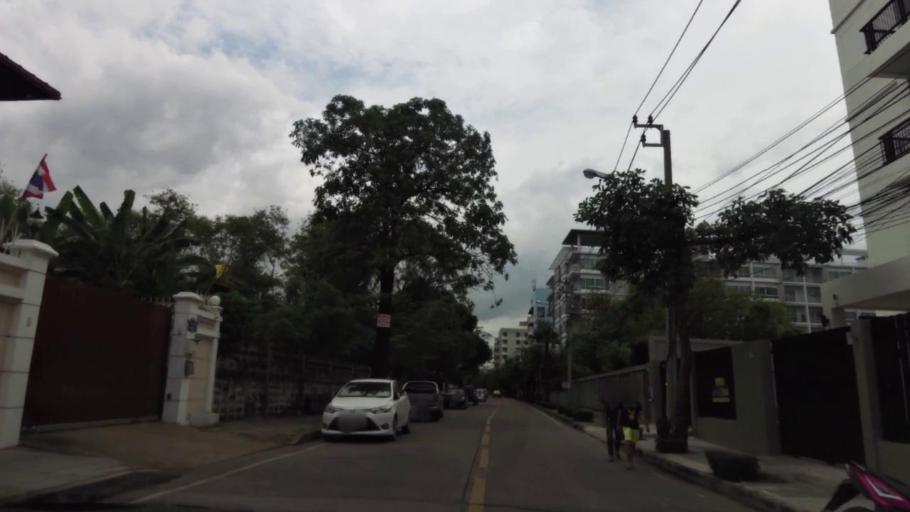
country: TH
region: Bangkok
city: Bang Kapi
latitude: 13.7541
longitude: 100.6397
